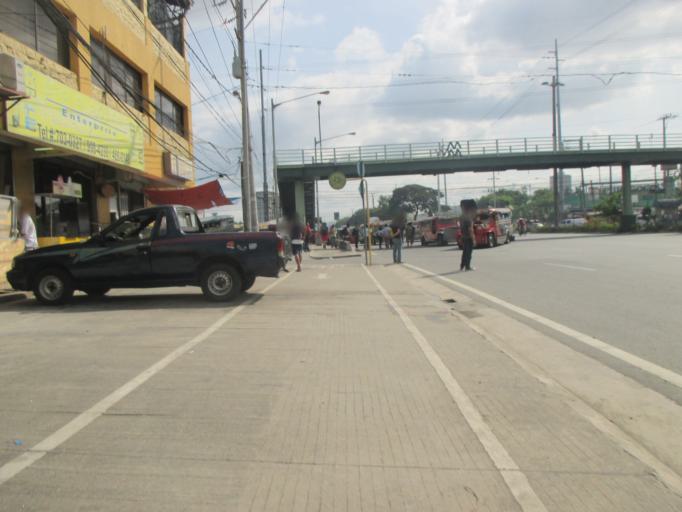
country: PH
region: Metro Manila
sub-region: Marikina
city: Calumpang
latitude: 14.6187
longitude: 121.0917
